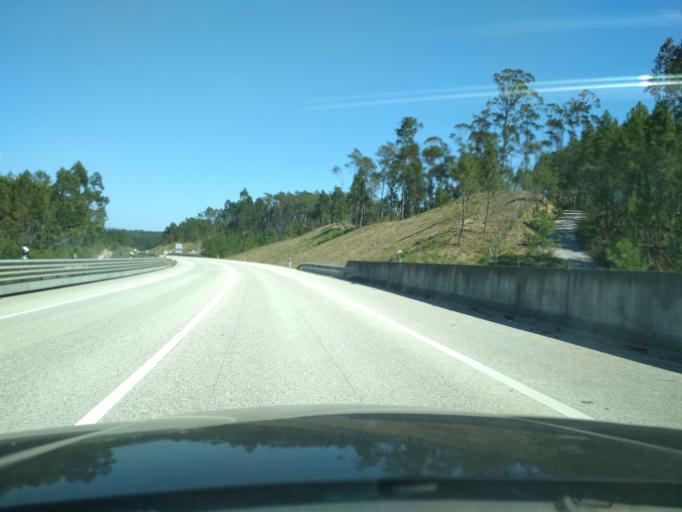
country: PT
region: Leiria
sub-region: Pombal
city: Lourical
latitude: 39.9860
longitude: -8.7509
